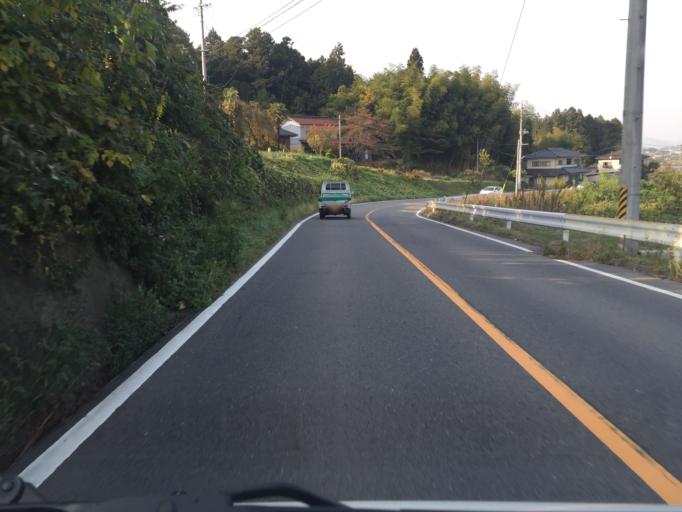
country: JP
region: Fukushima
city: Motomiya
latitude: 37.4702
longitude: 140.3895
